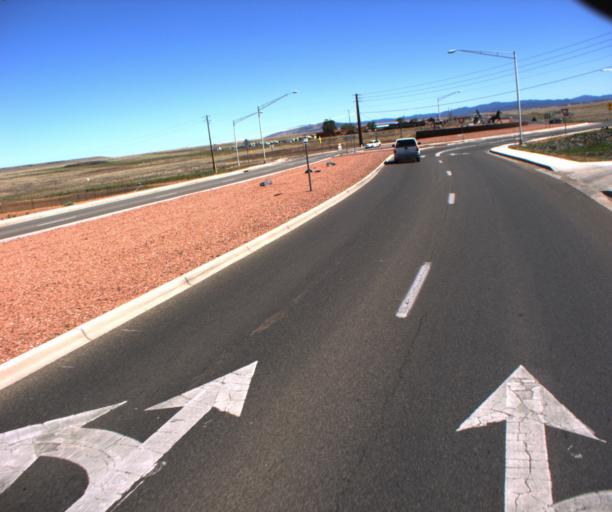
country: US
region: Arizona
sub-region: Yavapai County
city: Chino Valley
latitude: 34.7177
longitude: -112.4536
